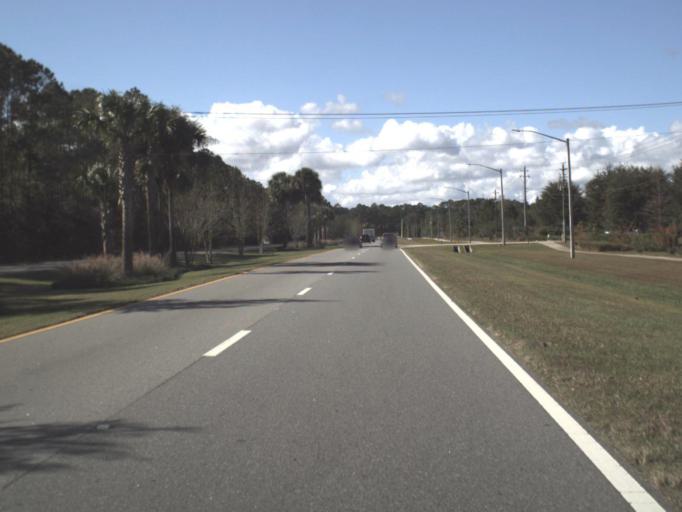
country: US
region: Florida
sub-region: Flagler County
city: Palm Coast
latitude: 29.5531
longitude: -81.2582
